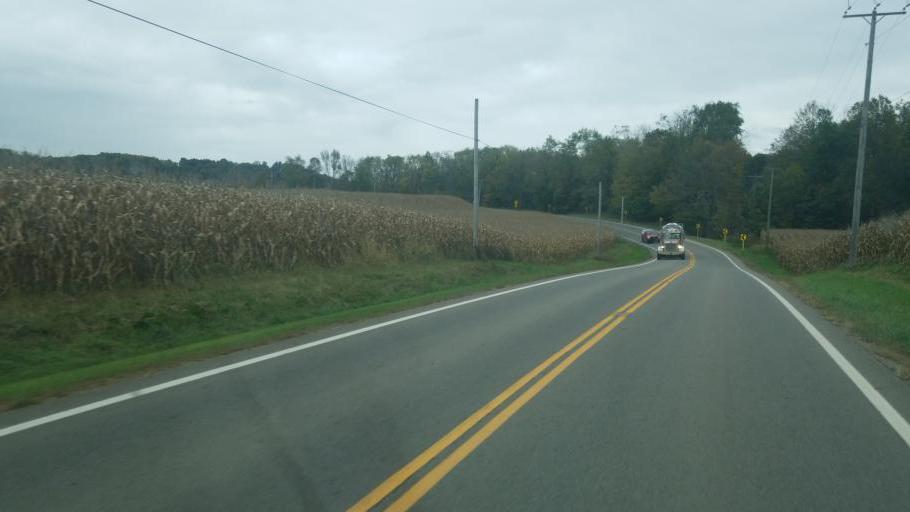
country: US
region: Ohio
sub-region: Richland County
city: Lincoln Heights
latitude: 40.7098
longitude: -82.3687
